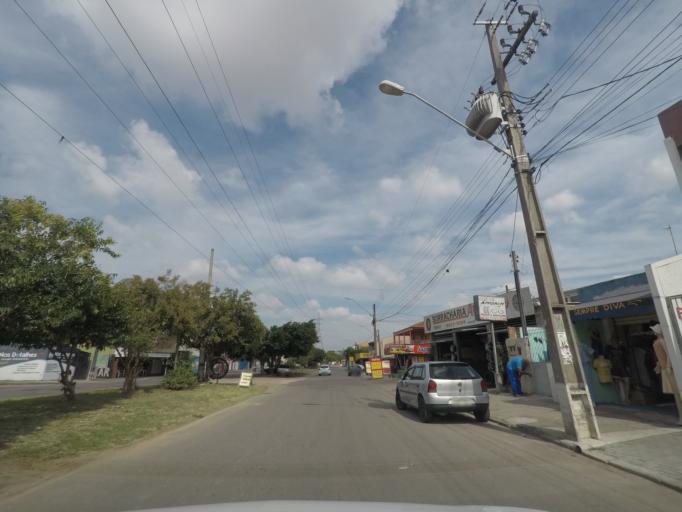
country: BR
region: Parana
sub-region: Pinhais
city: Pinhais
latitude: -25.4619
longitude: -49.1966
